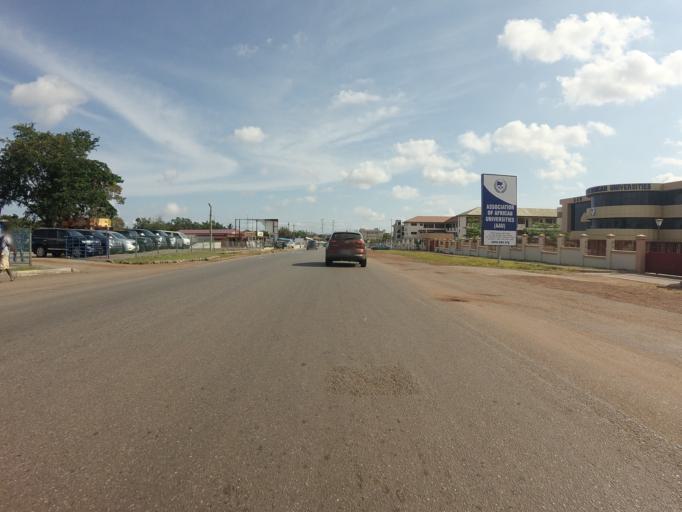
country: GH
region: Greater Accra
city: Medina Estates
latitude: 5.6467
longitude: -0.1696
